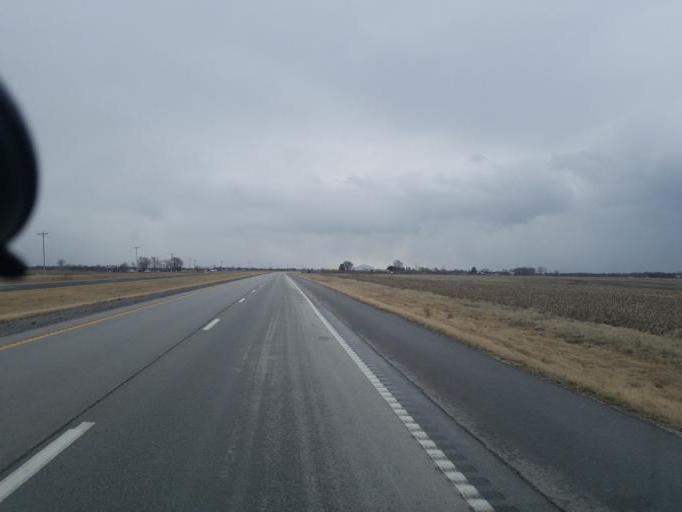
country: US
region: Missouri
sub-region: Macon County
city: Macon
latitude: 39.8224
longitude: -92.4730
